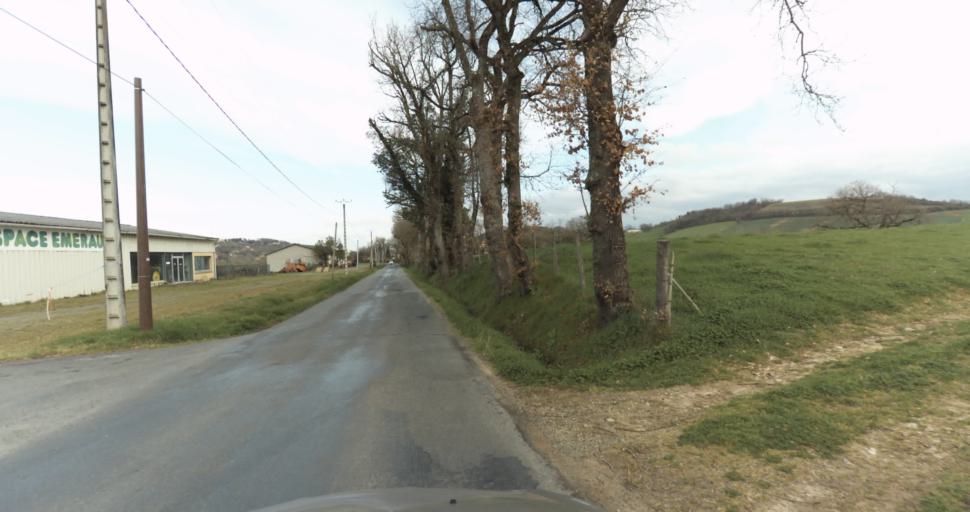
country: FR
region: Midi-Pyrenees
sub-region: Departement du Tarn
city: Puygouzon
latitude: 43.8888
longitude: 2.1933
